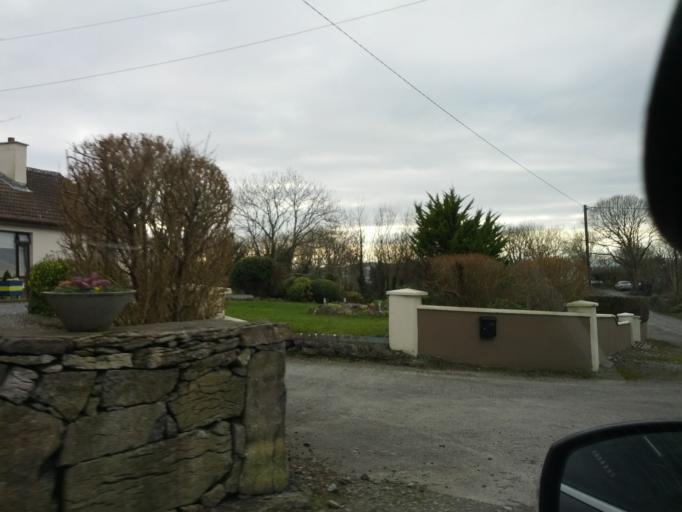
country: IE
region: Connaught
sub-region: County Galway
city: Oranmore
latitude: 53.1986
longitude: -8.9272
